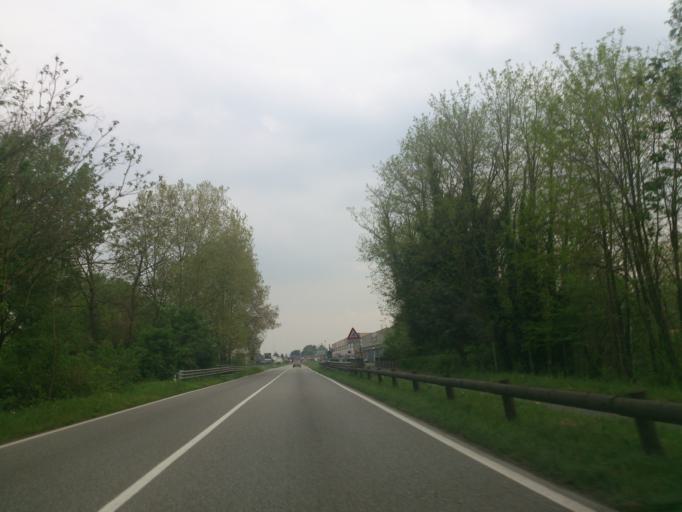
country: IT
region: Lombardy
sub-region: Citta metropolitana di Milano
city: Mezzate
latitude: 45.4481
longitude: 9.2878
